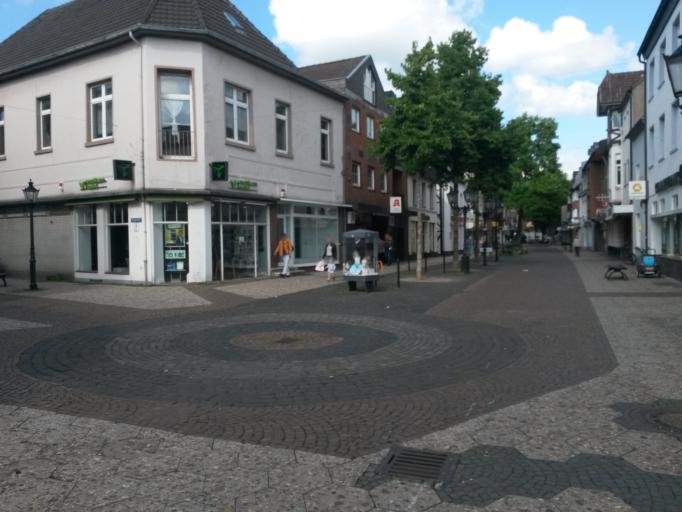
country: DE
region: North Rhine-Westphalia
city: Kempen
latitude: 51.3644
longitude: 6.4213
